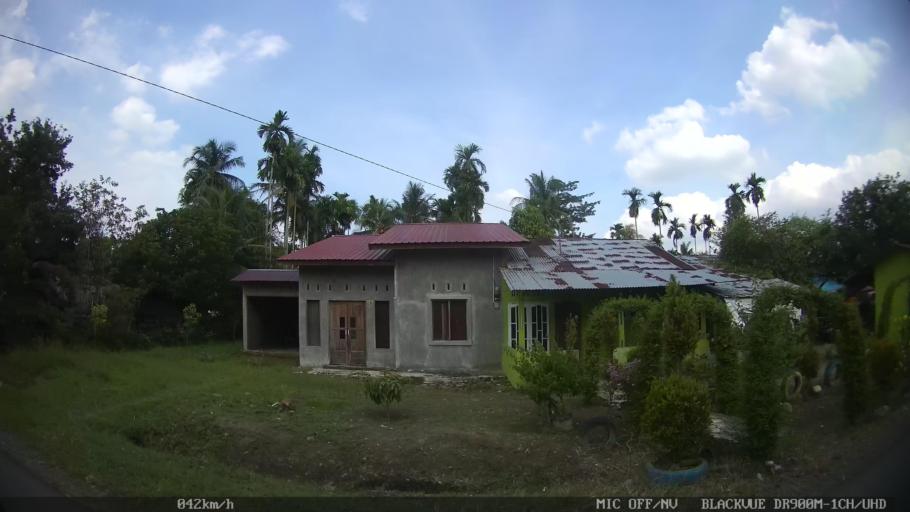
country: ID
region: North Sumatra
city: Binjai
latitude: 3.6376
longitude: 98.5175
